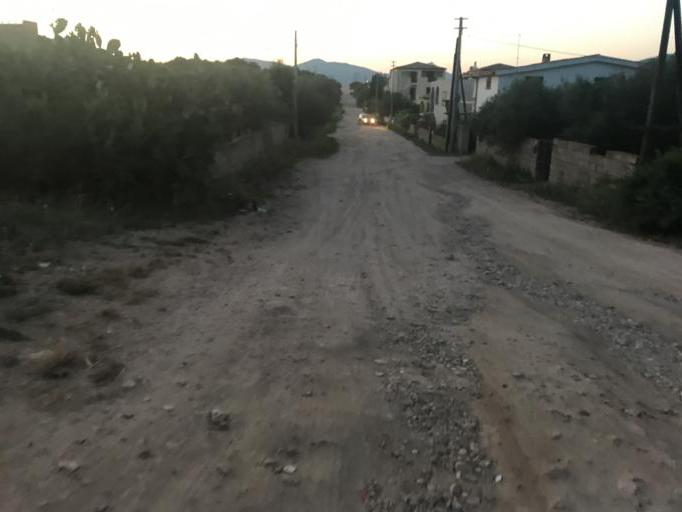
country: IT
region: Sardinia
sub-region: Provincia di Olbia-Tempio
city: Olbia
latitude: 40.9101
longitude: 9.5161
